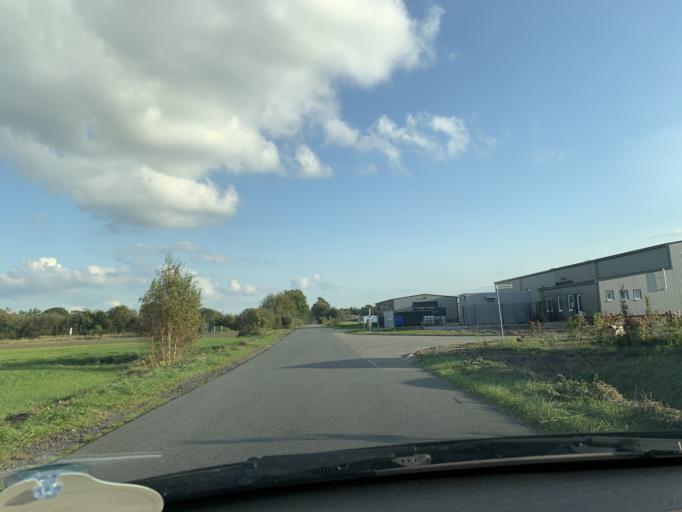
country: DE
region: Lower Saxony
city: Apen
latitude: 53.2505
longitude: 7.7733
